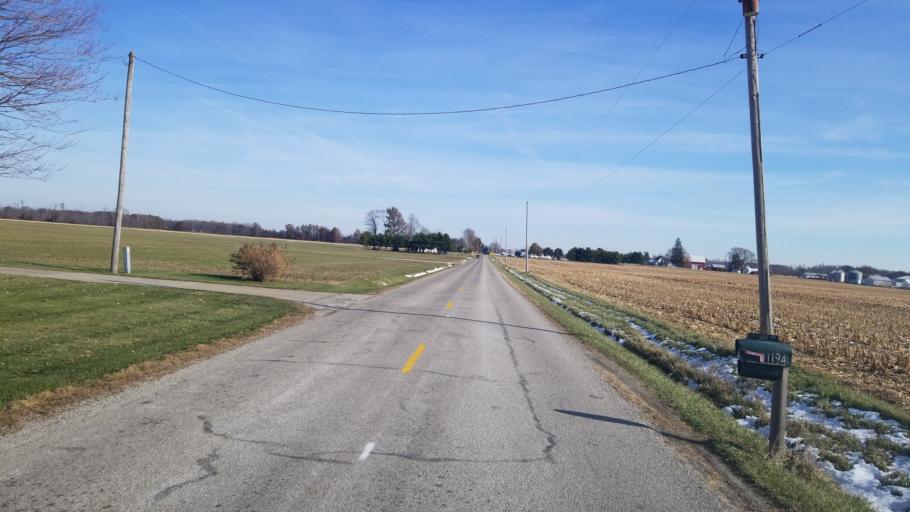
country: US
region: Ohio
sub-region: Huron County
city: Norwalk
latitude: 41.2042
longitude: -82.5477
